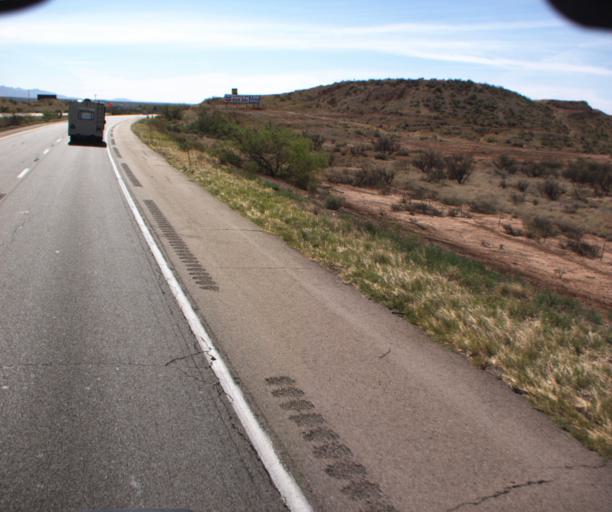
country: US
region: Arizona
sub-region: Cochise County
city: Benson
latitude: 31.9769
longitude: -110.2918
